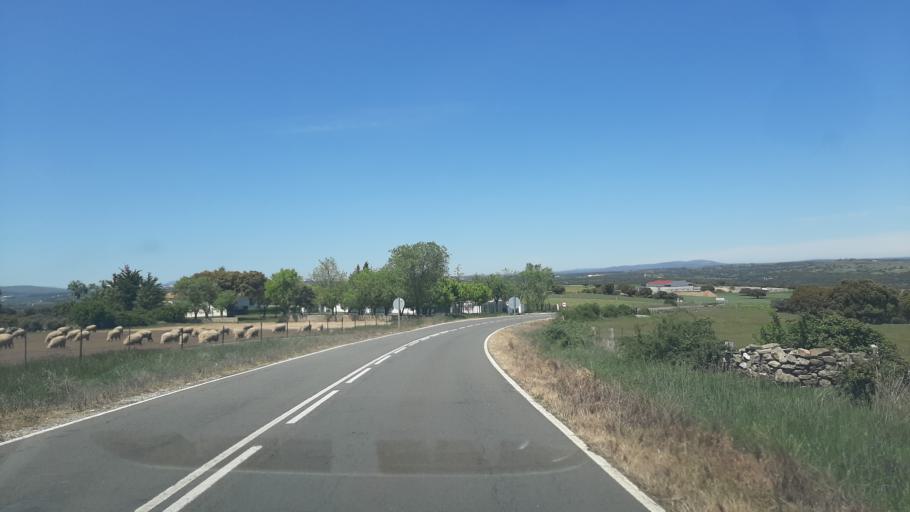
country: ES
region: Castille and Leon
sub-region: Provincia de Salamanca
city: Aldeavieja de Tormes
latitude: 40.5444
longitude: -5.5931
